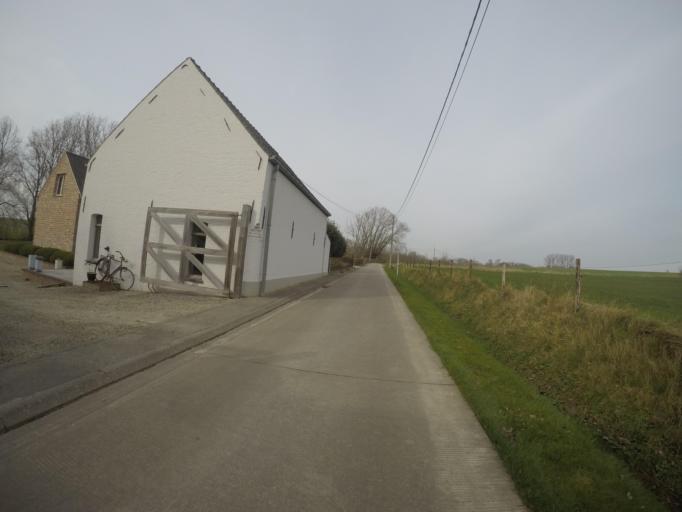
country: BE
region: Flanders
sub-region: Provincie Oost-Vlaanderen
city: Sint-Maria-Lierde
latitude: 50.8257
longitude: 3.8548
